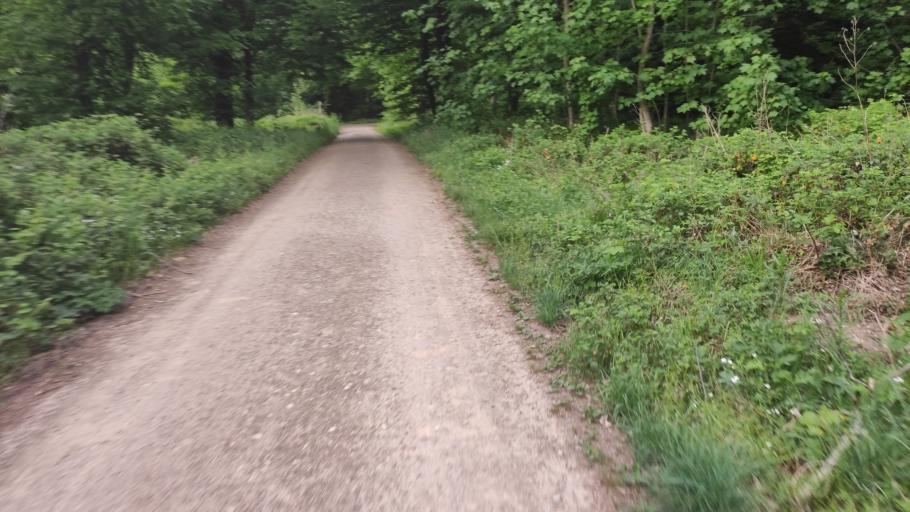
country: DE
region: Baden-Wuerttemberg
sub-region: Freiburg Region
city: Ebringen
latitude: 47.9838
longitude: 7.7700
